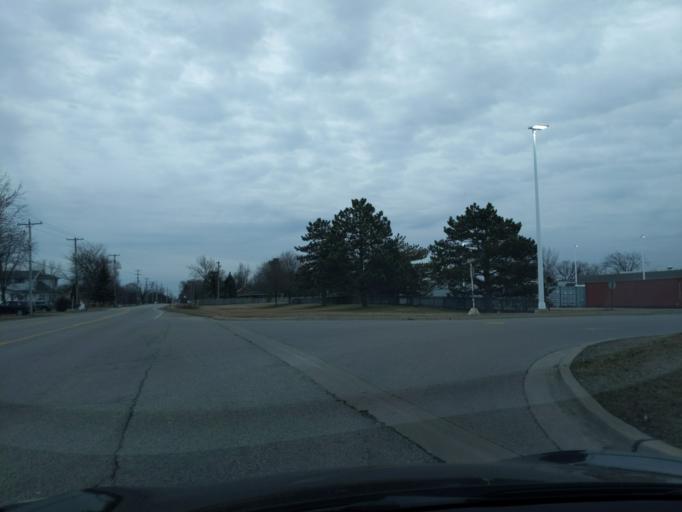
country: US
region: Michigan
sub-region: Bay County
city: Bay City
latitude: 43.6220
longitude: -83.9318
